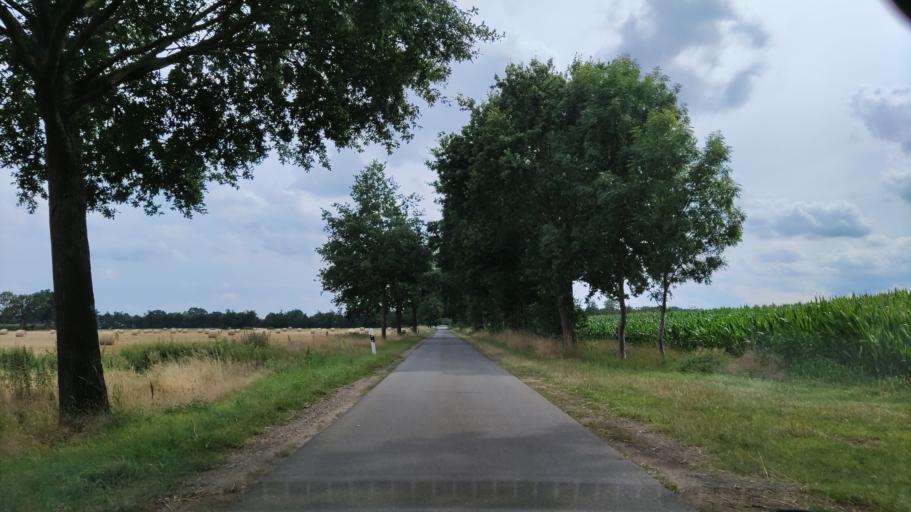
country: DE
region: Lower Saxony
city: Klein Gusborn
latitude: 53.0886
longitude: 11.1422
